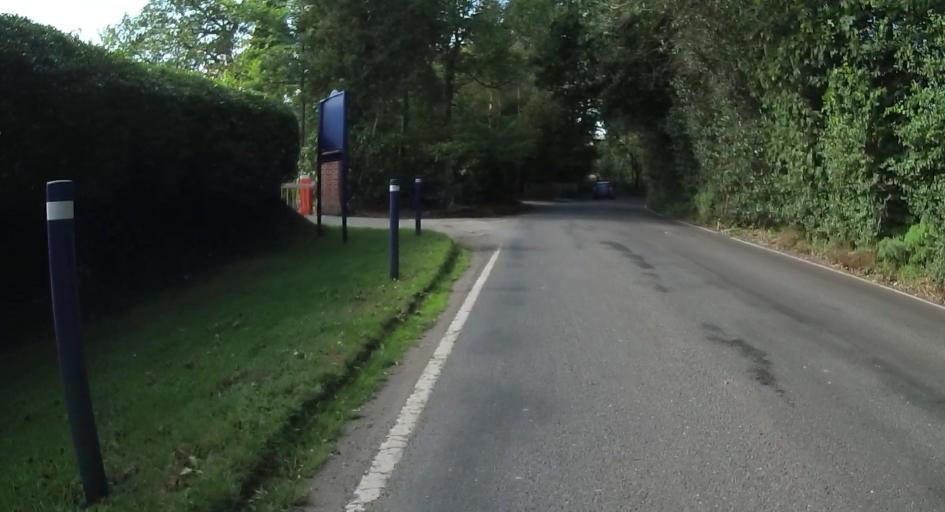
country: GB
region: England
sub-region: Surrey
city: Farnham
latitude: 51.1792
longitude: -0.7986
